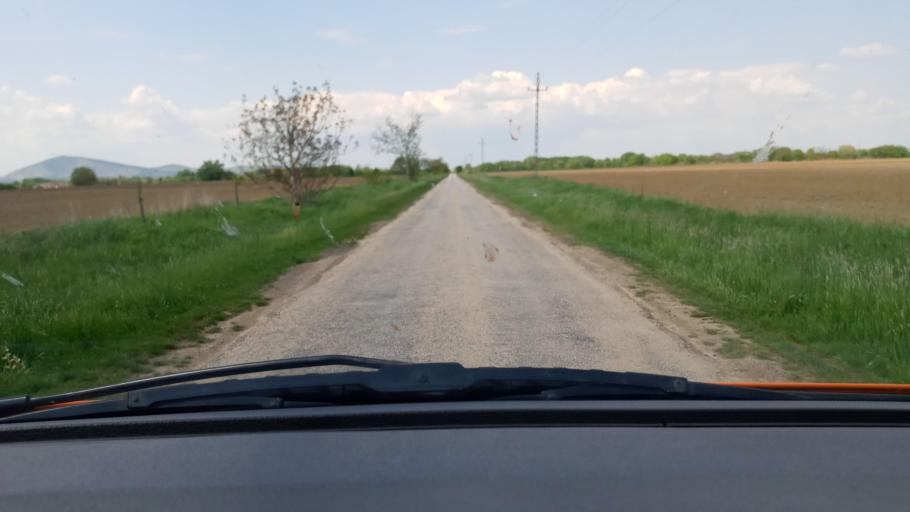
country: HU
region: Baranya
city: Villany
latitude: 45.8111
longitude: 18.5143
